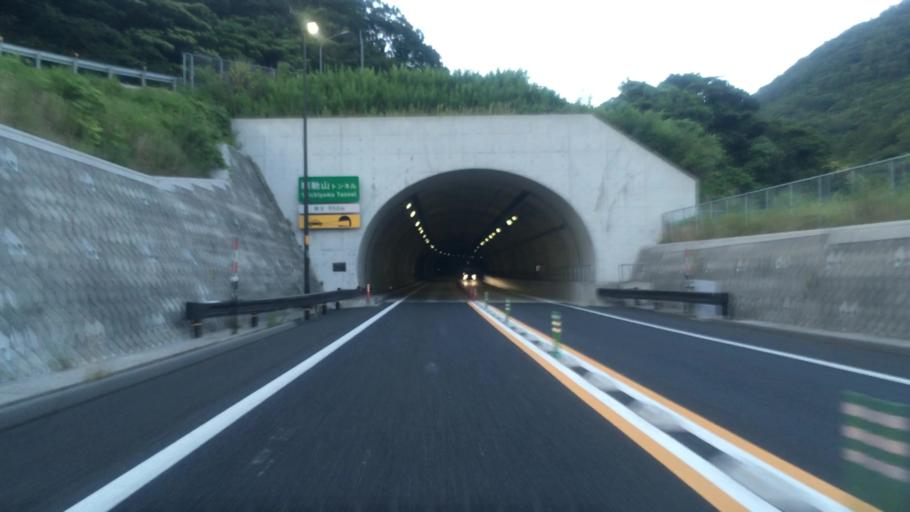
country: JP
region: Tottori
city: Tottori
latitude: 35.5608
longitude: 134.2846
